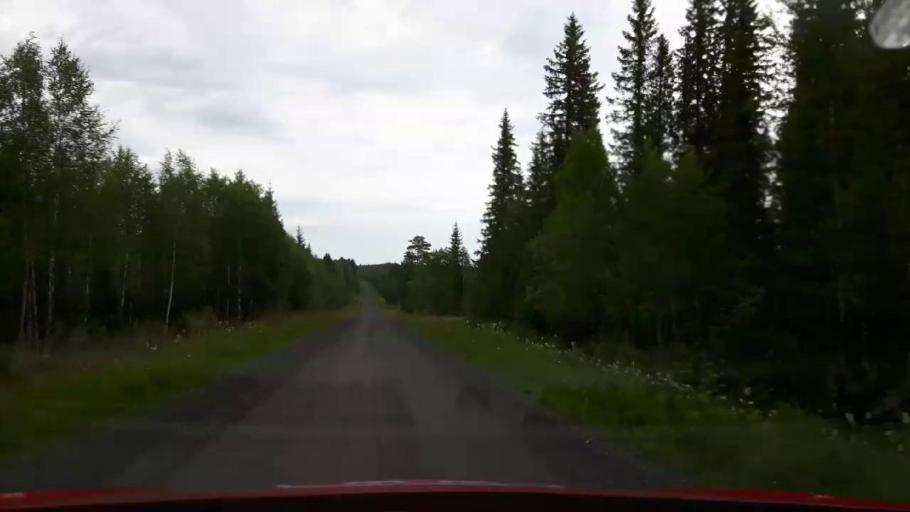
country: SE
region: Jaemtland
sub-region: OEstersunds Kommun
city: Lit
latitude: 63.3934
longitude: 15.2179
